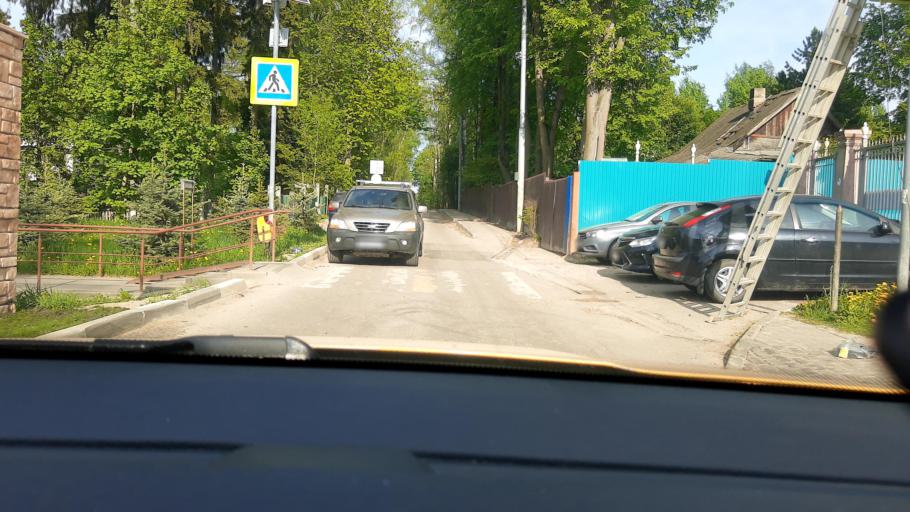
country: RU
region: Moskovskaya
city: Sheremet'yevskiy
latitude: 55.9546
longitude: 37.4426
